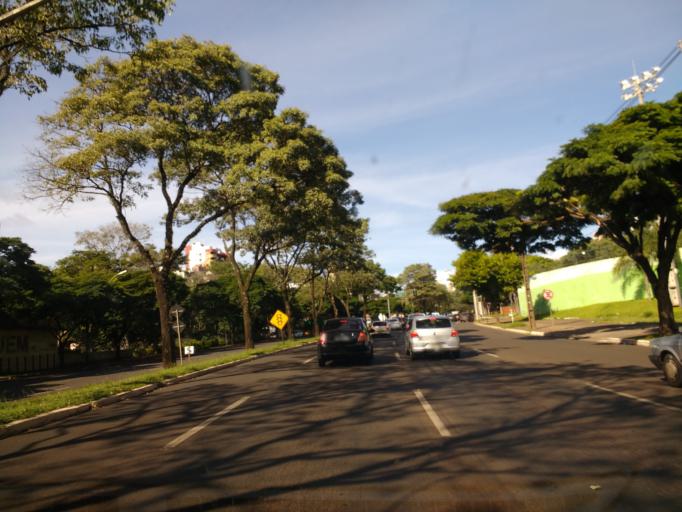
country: BR
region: Parana
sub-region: Maringa
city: Maringa
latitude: -23.4109
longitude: -51.9378
